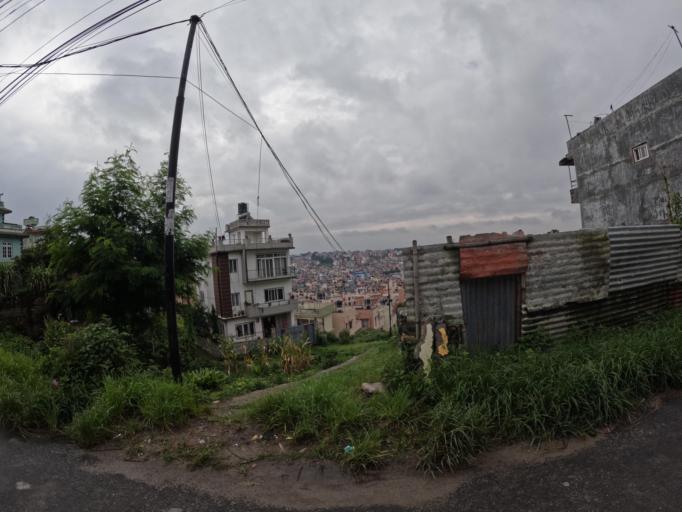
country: NP
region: Central Region
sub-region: Bagmati Zone
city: Kathmandu
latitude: 27.7539
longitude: 85.3213
